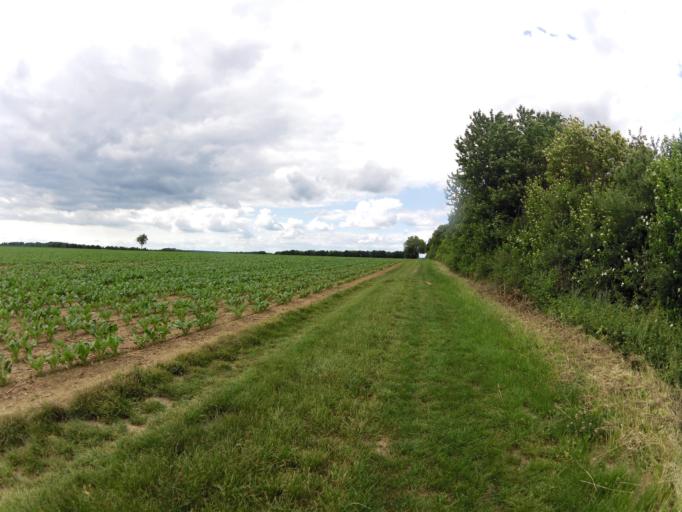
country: DE
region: Bavaria
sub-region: Regierungsbezirk Unterfranken
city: Gaukonigshofen
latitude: 49.6586
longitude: 10.0104
